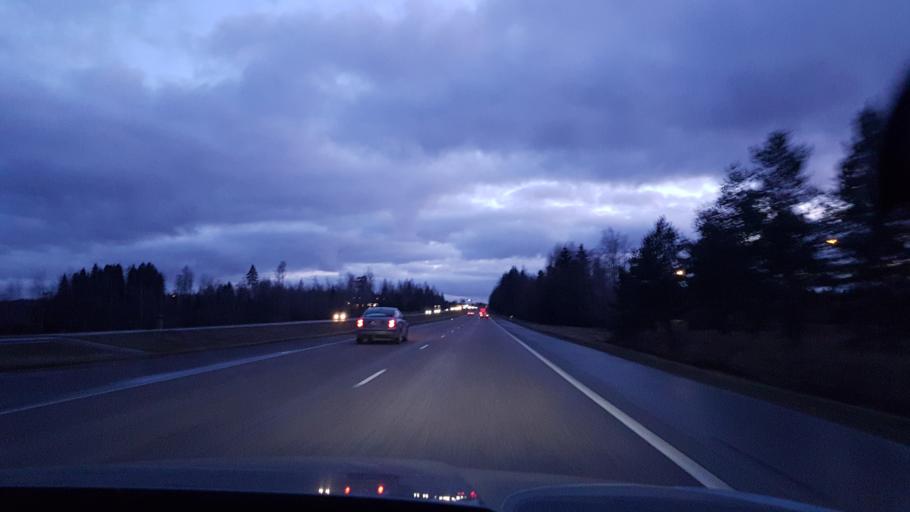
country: FI
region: Uusimaa
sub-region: Helsinki
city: Nurmijaervi
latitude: 60.5124
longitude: 24.8474
